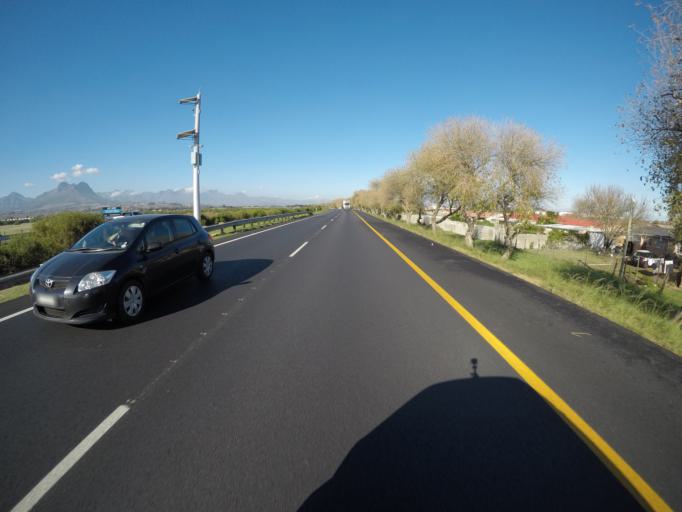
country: ZA
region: Western Cape
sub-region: Cape Winelands District Municipality
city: Stellenbosch
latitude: -34.0566
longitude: 18.7701
